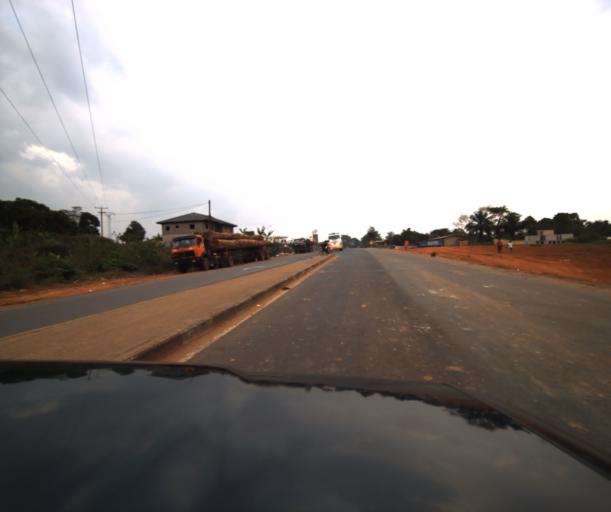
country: CM
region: Centre
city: Mbankomo
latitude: 3.7890
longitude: 11.4222
